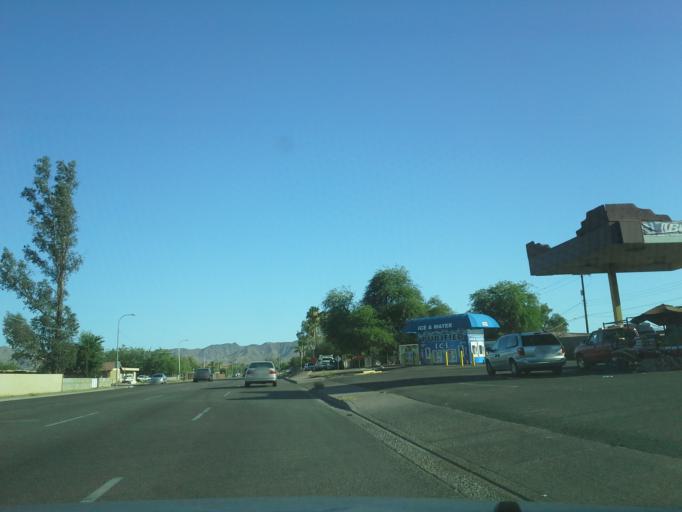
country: US
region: Arizona
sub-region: Maricopa County
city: Phoenix
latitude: 33.4053
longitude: -112.0995
